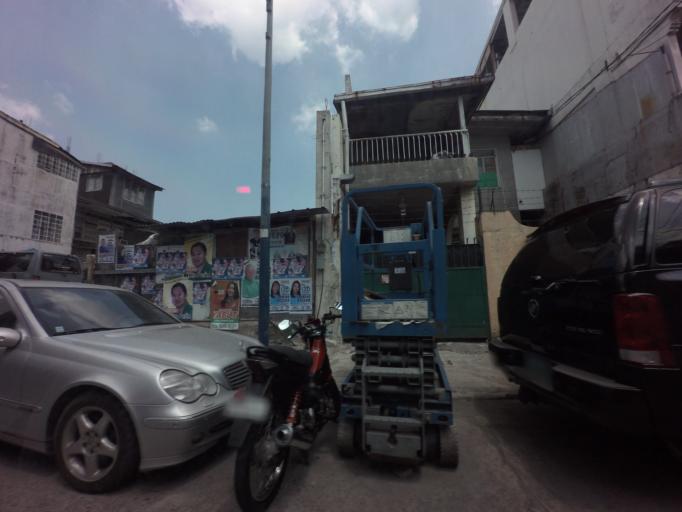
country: PH
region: Metro Manila
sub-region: Mandaluyong
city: Mandaluyong City
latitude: 14.5710
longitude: 121.0248
